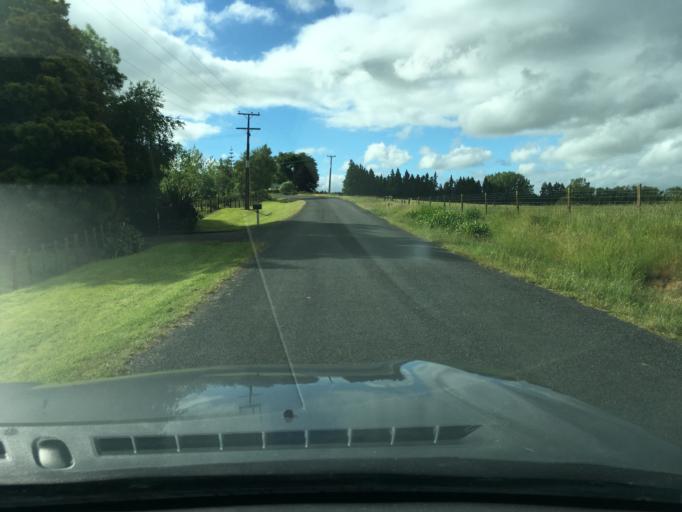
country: NZ
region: Waikato
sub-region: Hamilton City
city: Hamilton
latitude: -37.8258
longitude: 175.1774
